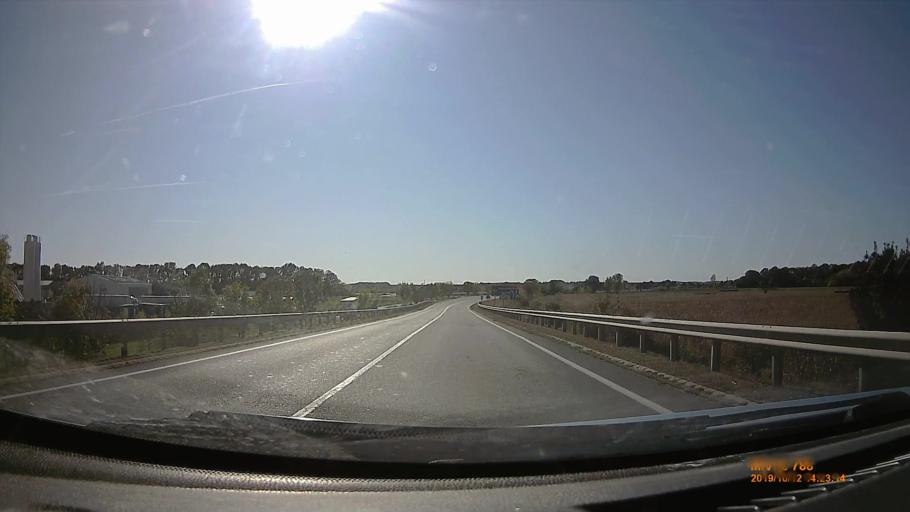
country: HU
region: Hajdu-Bihar
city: Biharkeresztes
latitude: 47.1368
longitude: 21.7033
